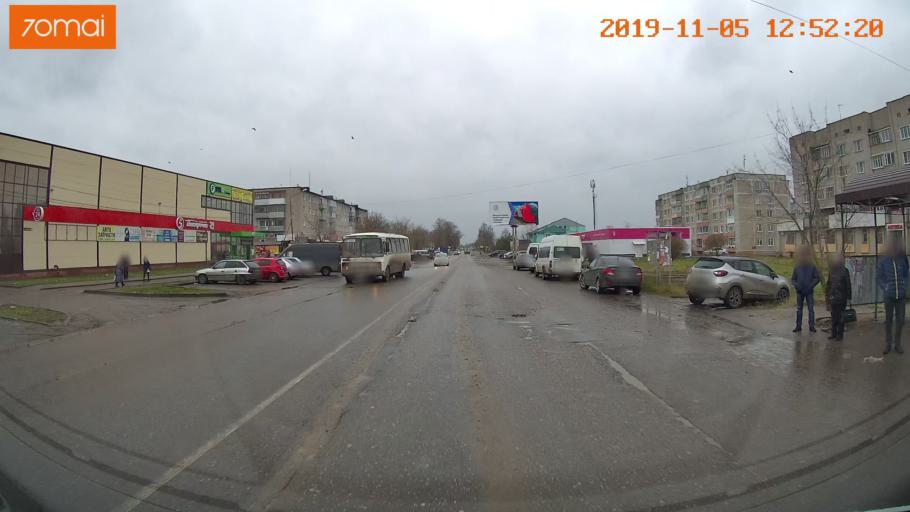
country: RU
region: Ivanovo
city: Kokhma
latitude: 56.9403
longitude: 41.1079
